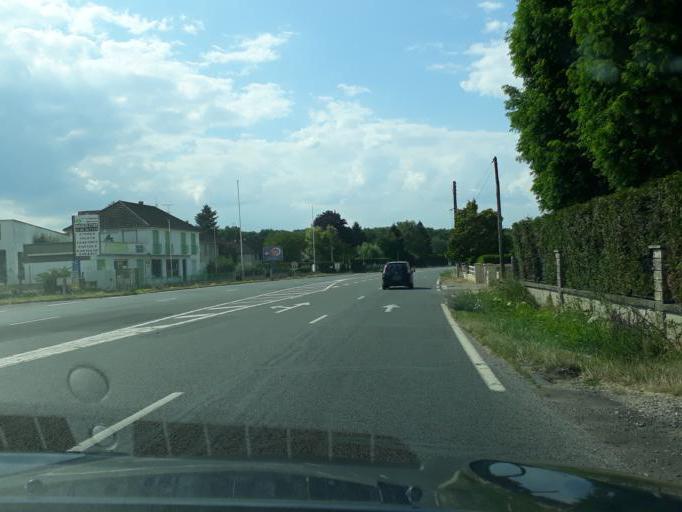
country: FR
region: Bourgogne
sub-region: Departement de la Nievre
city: Marzy
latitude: 47.0010
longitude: 3.1008
